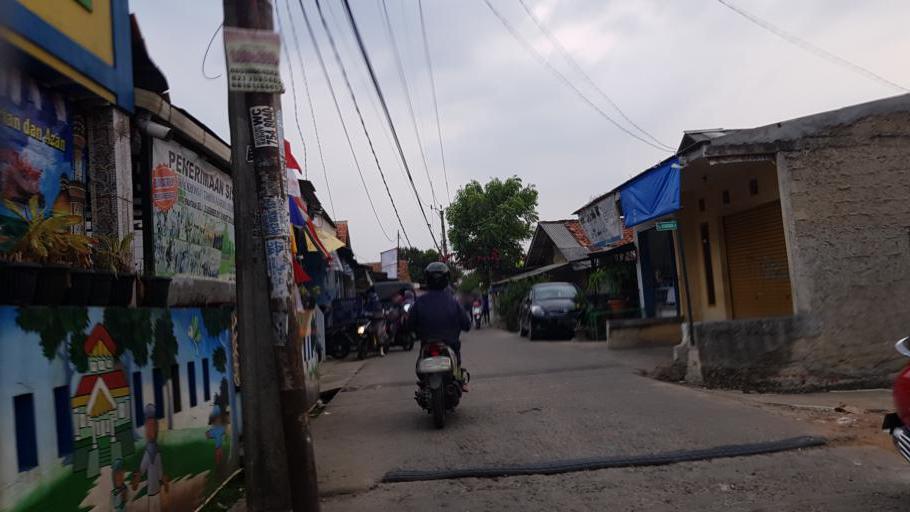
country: ID
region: West Java
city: Sawangan
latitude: -6.3801
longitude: 106.7934
